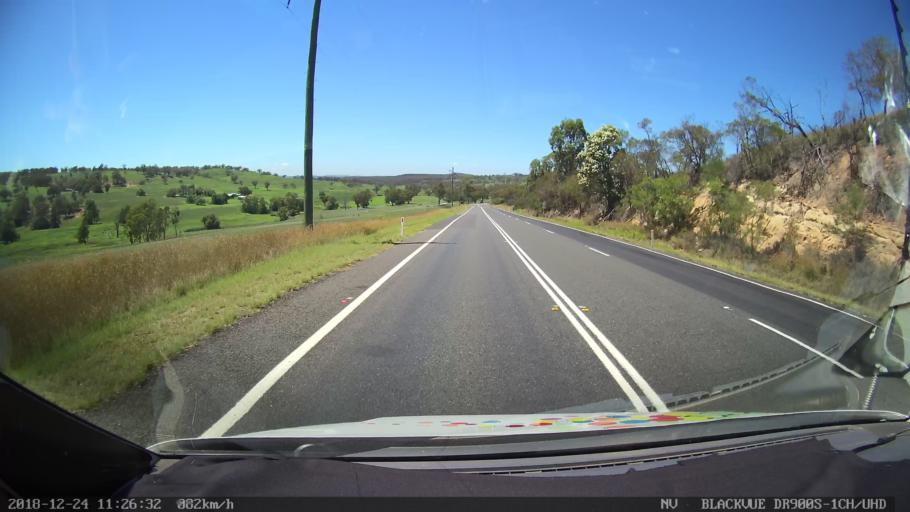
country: AU
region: New South Wales
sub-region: Upper Hunter Shire
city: Merriwa
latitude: -32.1704
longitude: 150.4319
